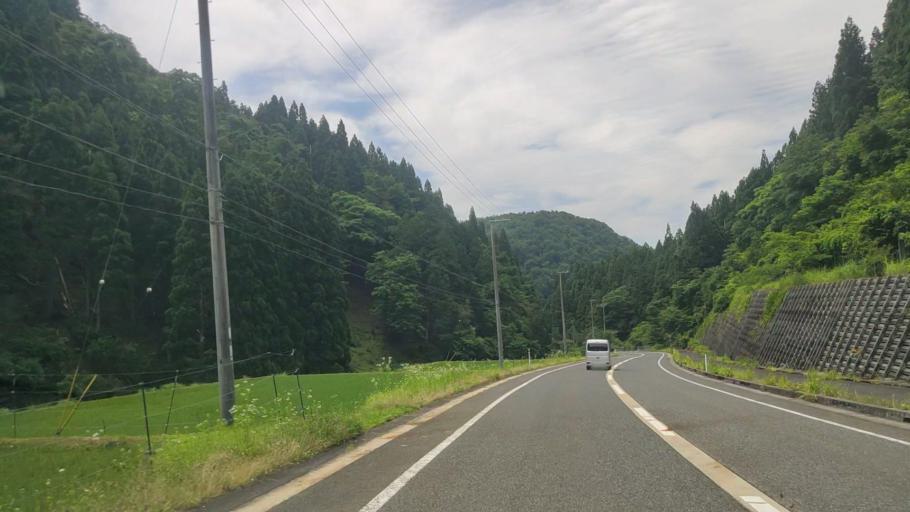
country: JP
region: Hyogo
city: Toyooka
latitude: 35.4861
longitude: 134.6155
